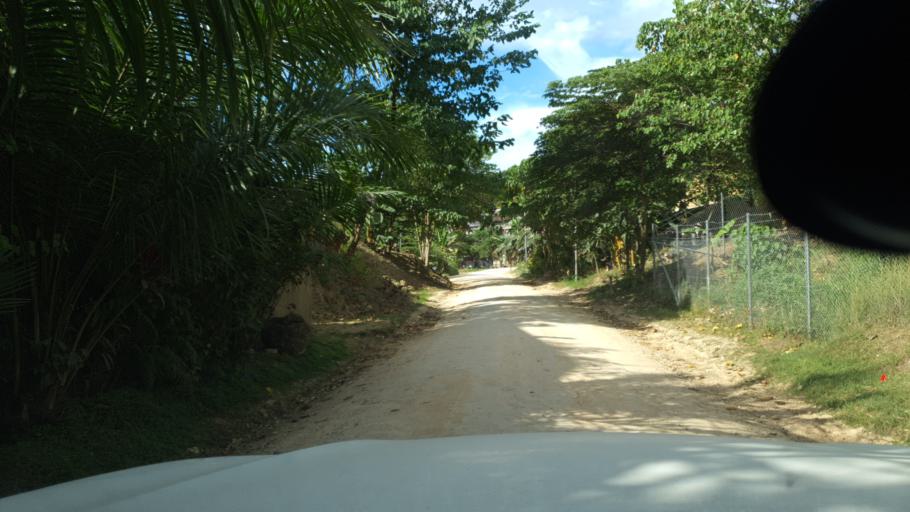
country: SB
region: Guadalcanal
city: Honiara
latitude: -9.4350
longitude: 159.9322
